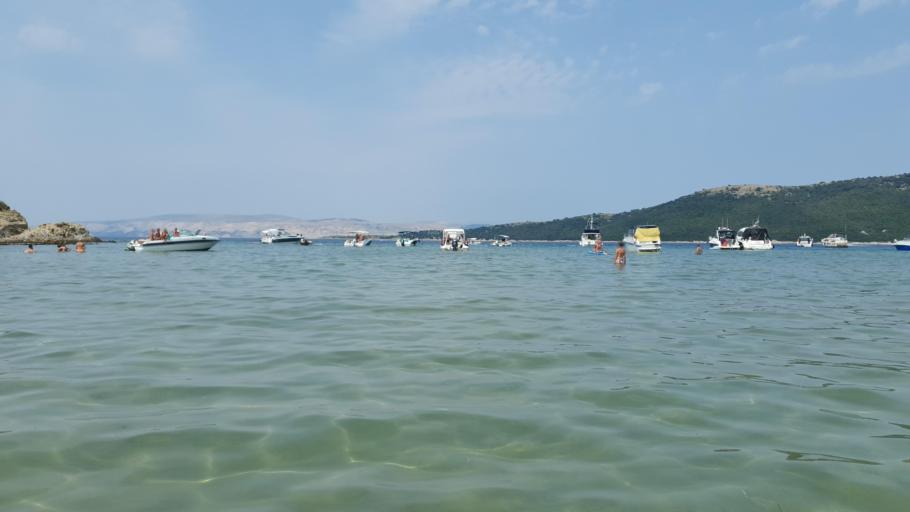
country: HR
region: Primorsko-Goranska
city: Lopar
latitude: 44.8465
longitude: 14.7390
